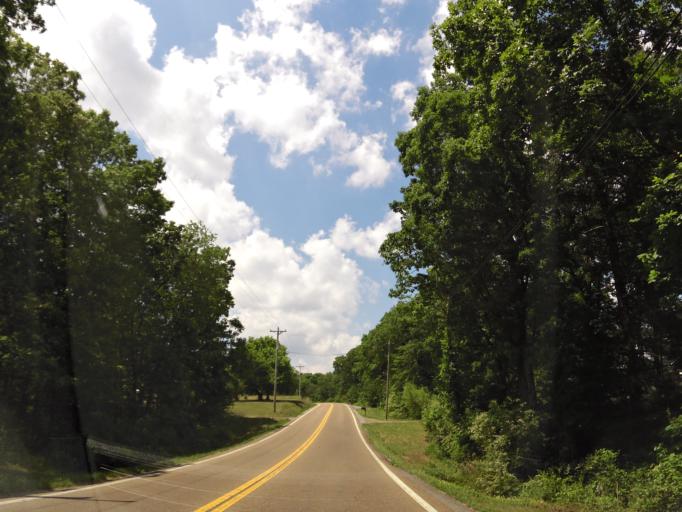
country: US
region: Tennessee
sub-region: Bledsoe County
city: Pikeville
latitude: 35.5776
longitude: -85.1187
